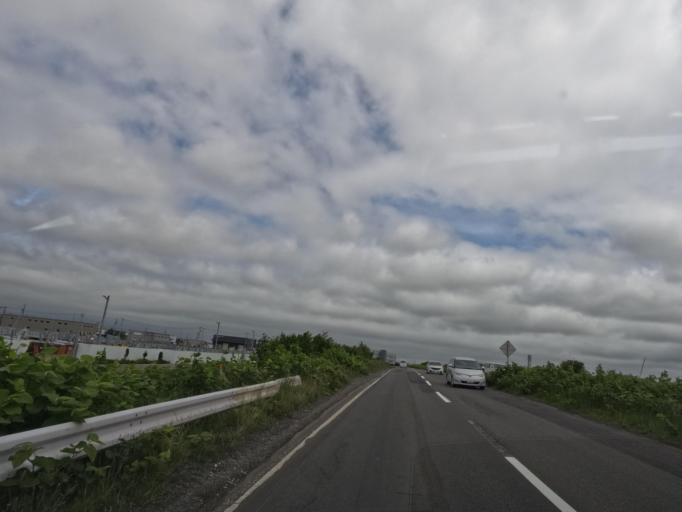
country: JP
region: Hokkaido
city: Sapporo
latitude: 43.0858
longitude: 141.4189
